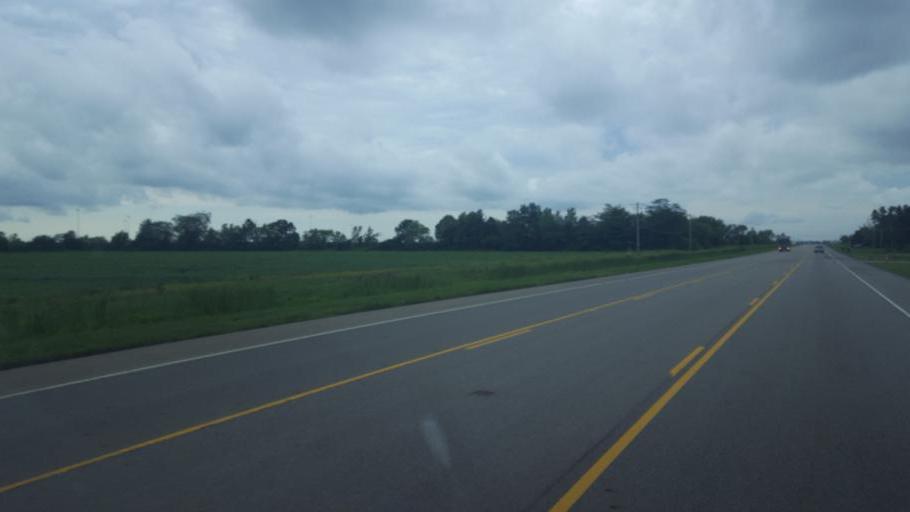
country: US
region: Ohio
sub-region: Pickaway County
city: Ashville
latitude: 39.7770
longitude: -82.9489
